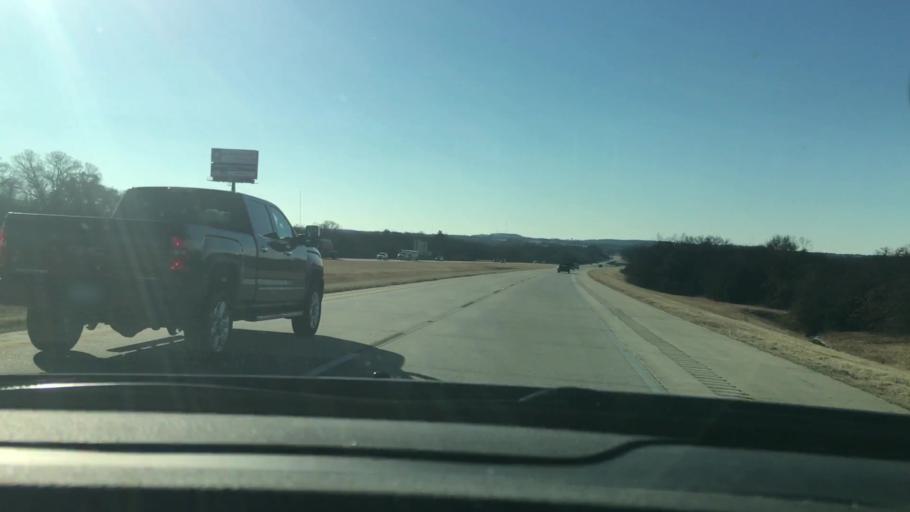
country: US
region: Oklahoma
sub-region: Carter County
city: Ardmore
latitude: 34.0551
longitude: -97.1490
